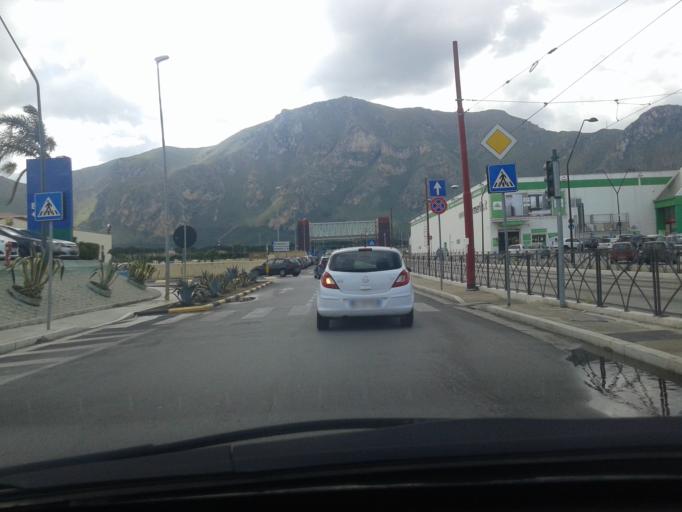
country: IT
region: Sicily
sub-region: Palermo
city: Ciaculli
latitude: 38.0910
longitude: 13.4104
